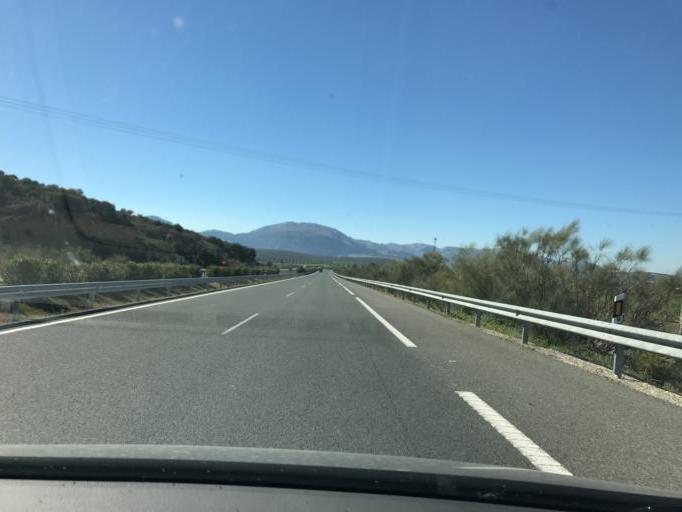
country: ES
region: Andalusia
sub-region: Provincia de Malaga
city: Villanueva del Trabuco
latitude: 37.0951
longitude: -4.3158
